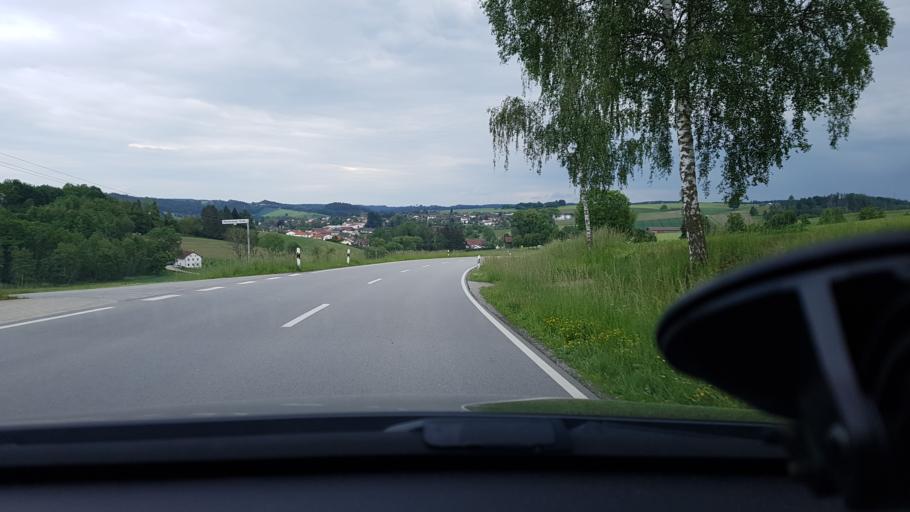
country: DE
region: Bavaria
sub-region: Lower Bavaria
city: Triftern
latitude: 48.4005
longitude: 12.9913
